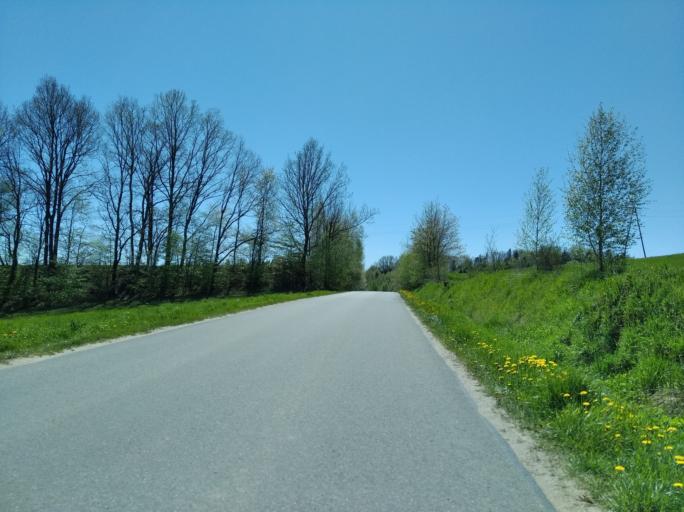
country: PL
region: Subcarpathian Voivodeship
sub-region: Powiat debicki
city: Brzostek
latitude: 49.9061
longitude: 21.4071
